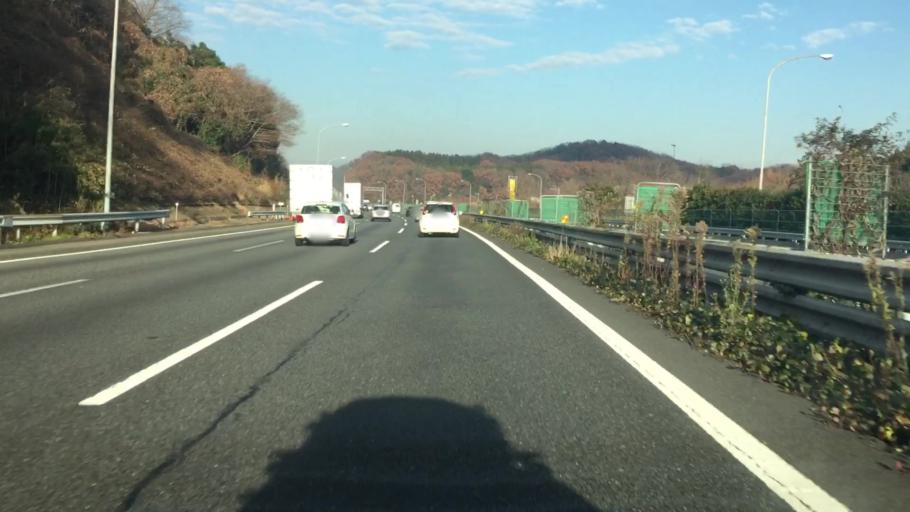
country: JP
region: Saitama
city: Ogawa
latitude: 36.0824
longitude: 139.2971
